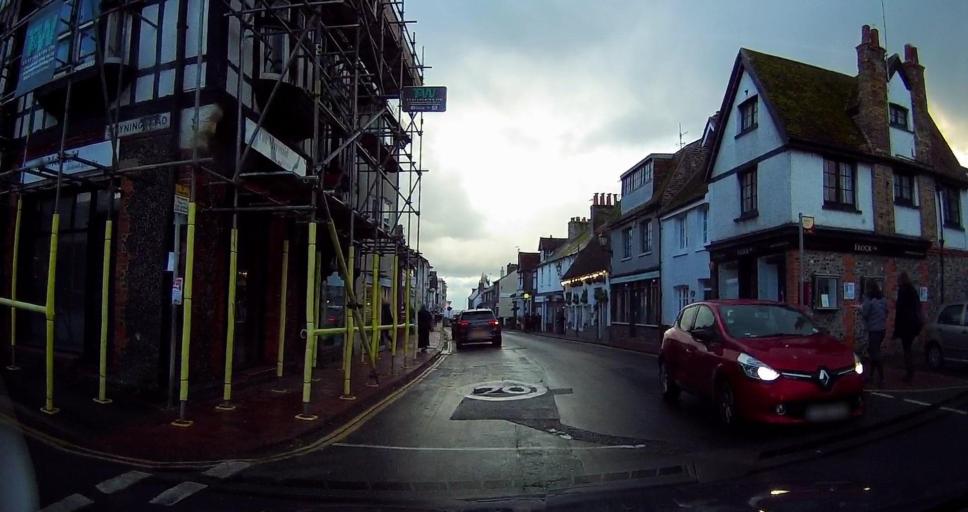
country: GB
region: England
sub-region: Brighton and Hove
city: Rottingdean
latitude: 50.8050
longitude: -0.0581
